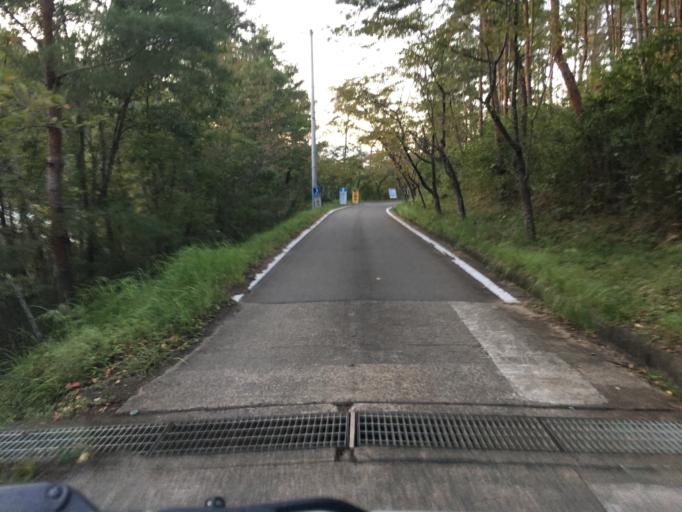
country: JP
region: Fukushima
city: Yanagawamachi-saiwaicho
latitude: 37.8496
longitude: 140.6316
